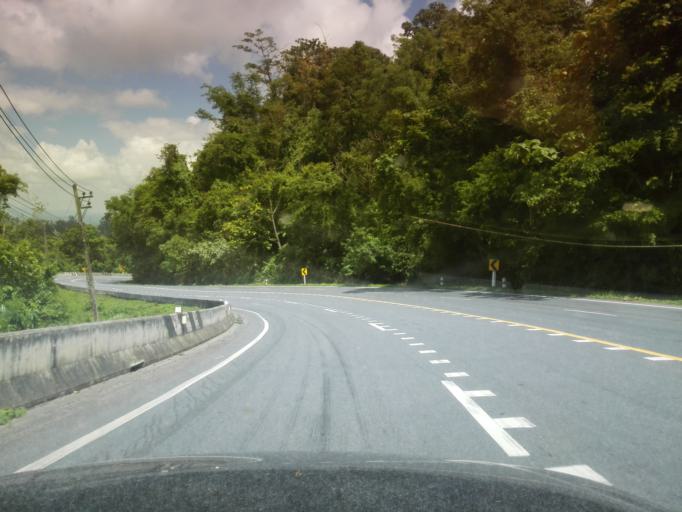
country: TH
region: Tak
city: Mae Sot
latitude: 16.7705
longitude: 98.6897
